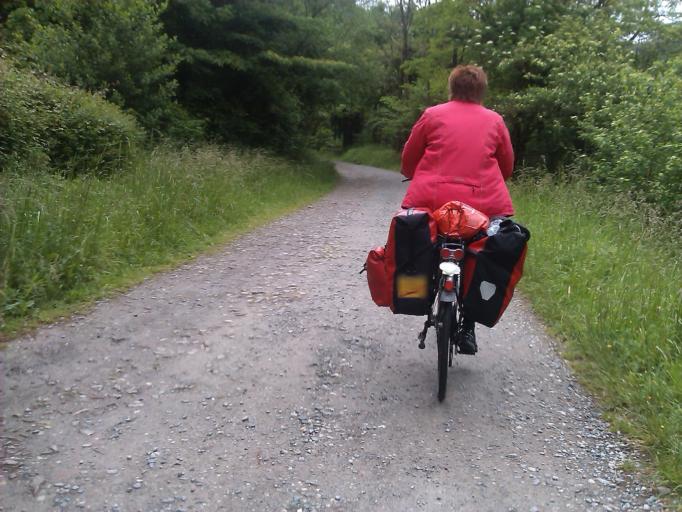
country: ES
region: Basque Country
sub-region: Provincia de Guipuzcoa
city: Andoain
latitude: 43.1933
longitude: -2.0079
